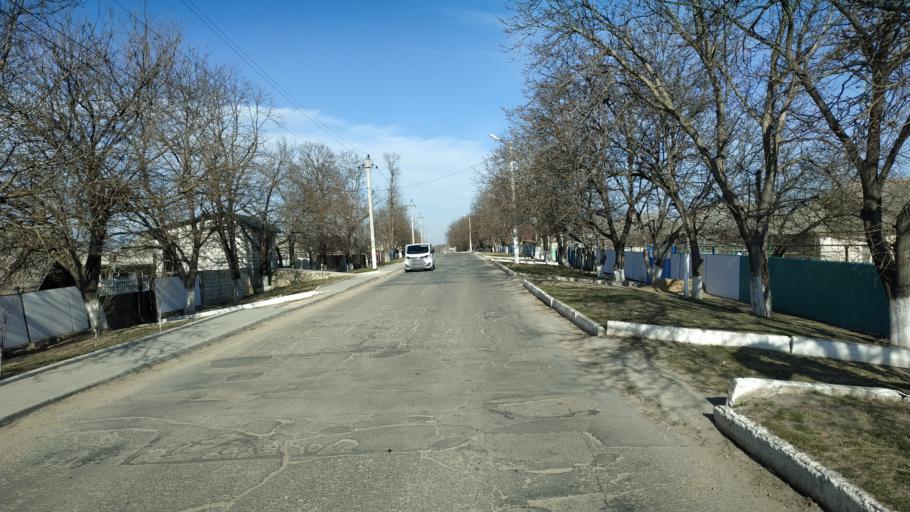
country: MD
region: Chisinau
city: Vatra
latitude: 47.0154
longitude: 28.6561
